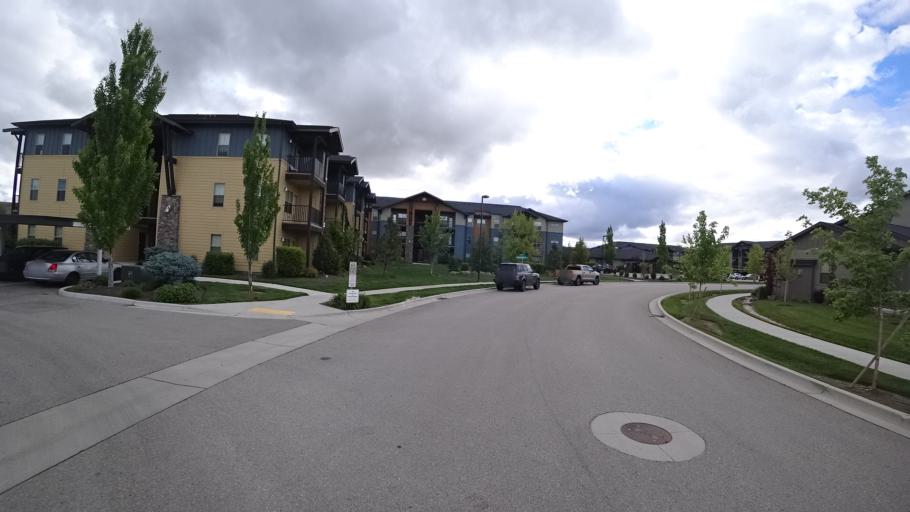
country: US
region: Idaho
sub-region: Ada County
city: Eagle
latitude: 43.6769
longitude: -116.2921
